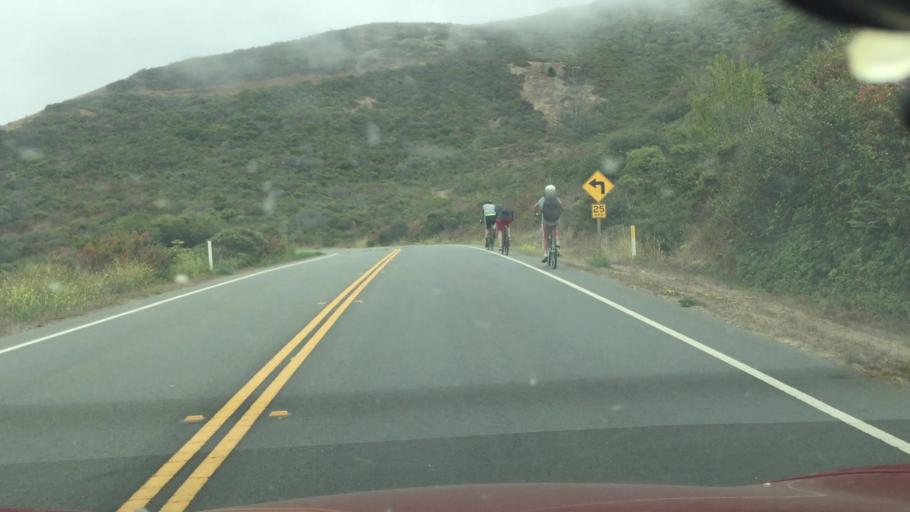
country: US
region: California
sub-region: Marin County
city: Sausalito
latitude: 37.8337
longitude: -122.5060
